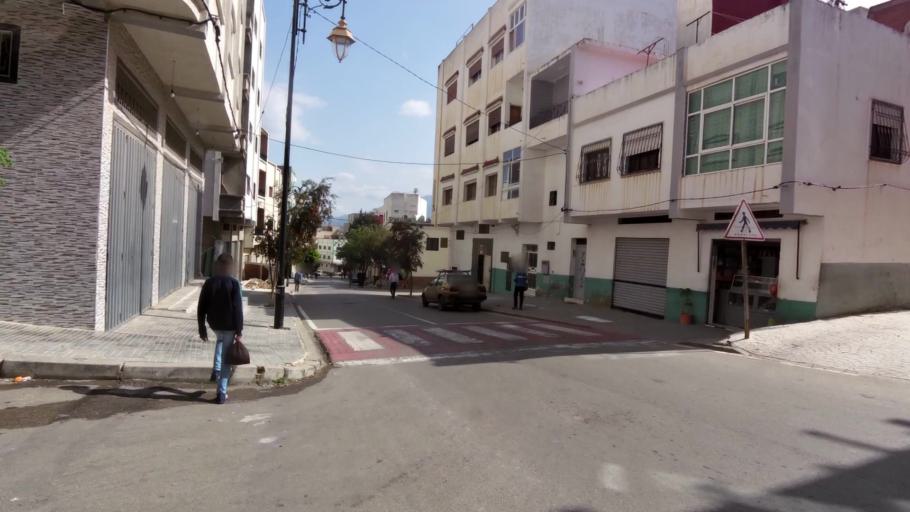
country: MA
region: Tanger-Tetouan
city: Tetouan
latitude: 35.5854
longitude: -5.3588
